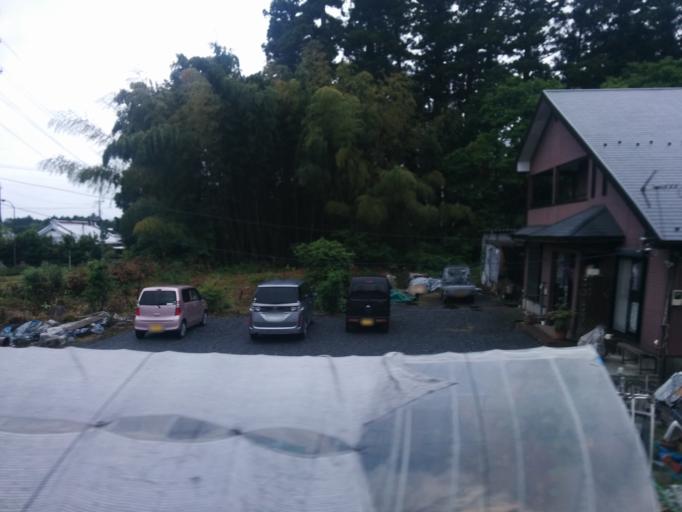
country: JP
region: Tochigi
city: Kanuma
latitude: 36.6187
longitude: 139.7362
